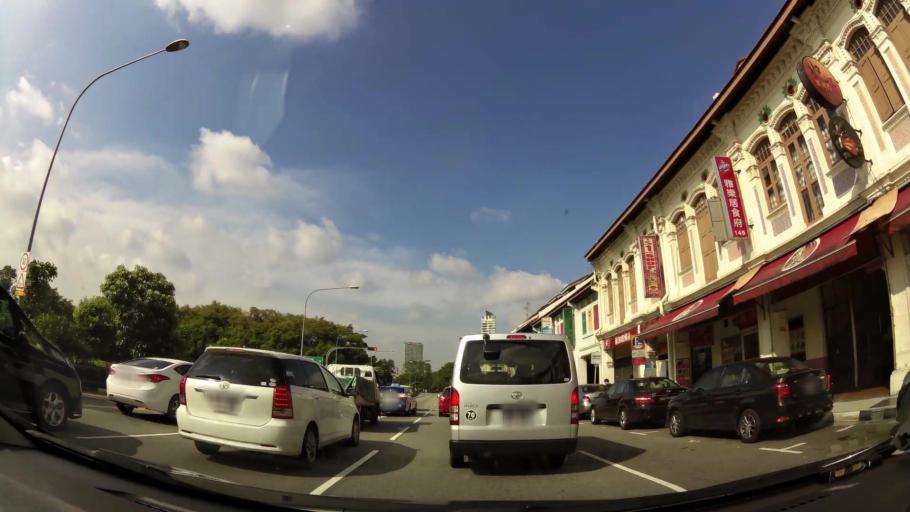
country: SG
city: Singapore
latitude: 1.3111
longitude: 103.8743
